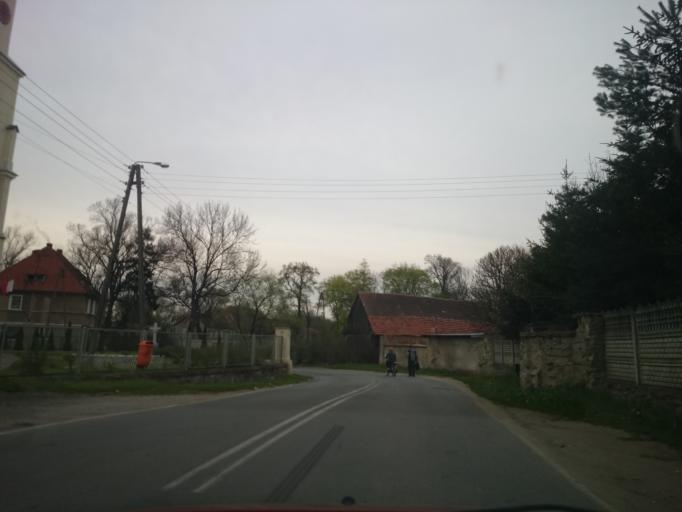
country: PL
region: Lower Silesian Voivodeship
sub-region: Powiat strzelinski
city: Przeworno
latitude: 50.6452
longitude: 17.1725
